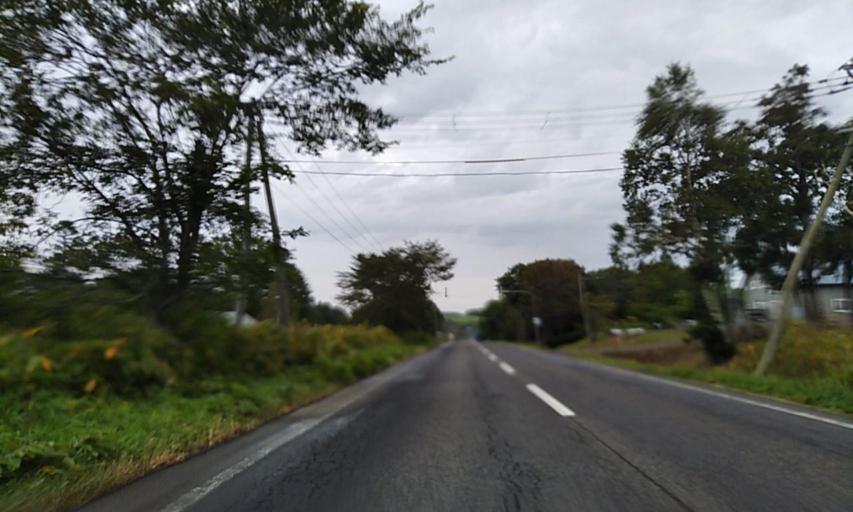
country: JP
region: Hokkaido
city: Mombetsu
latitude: 44.5307
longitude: 143.0388
